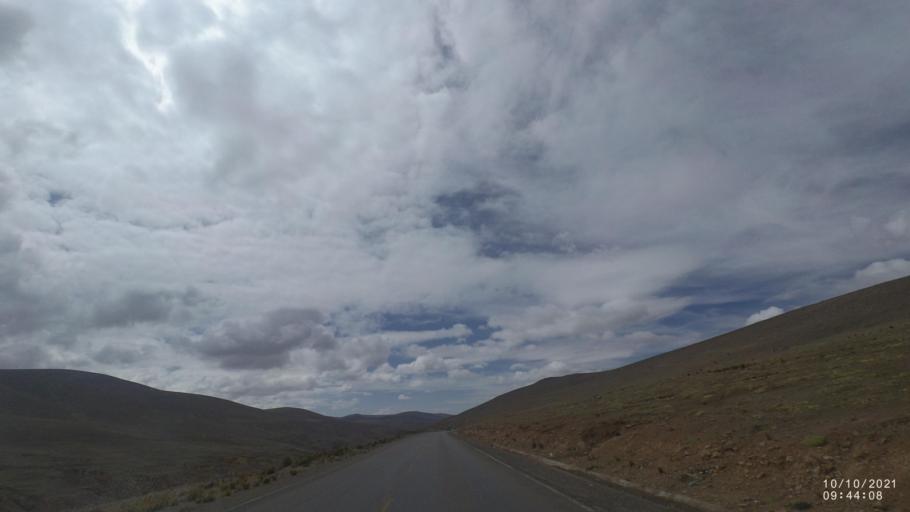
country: BO
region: La Paz
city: Quime
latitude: -17.1572
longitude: -67.3407
